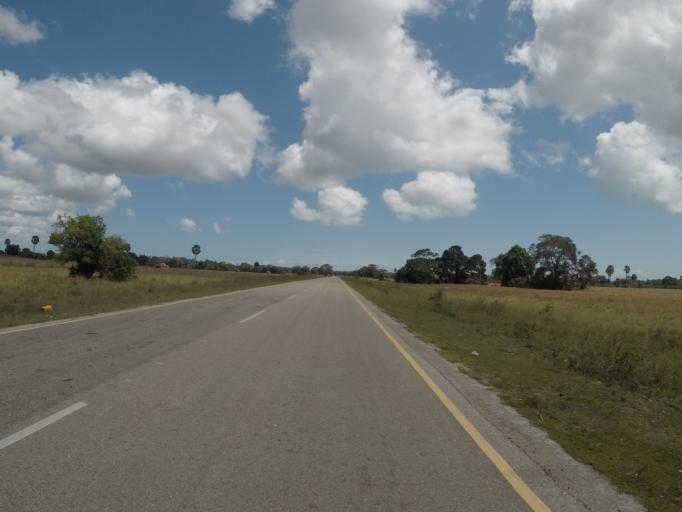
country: TZ
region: Zanzibar Central/South
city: Koani
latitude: -6.2186
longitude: 39.3636
